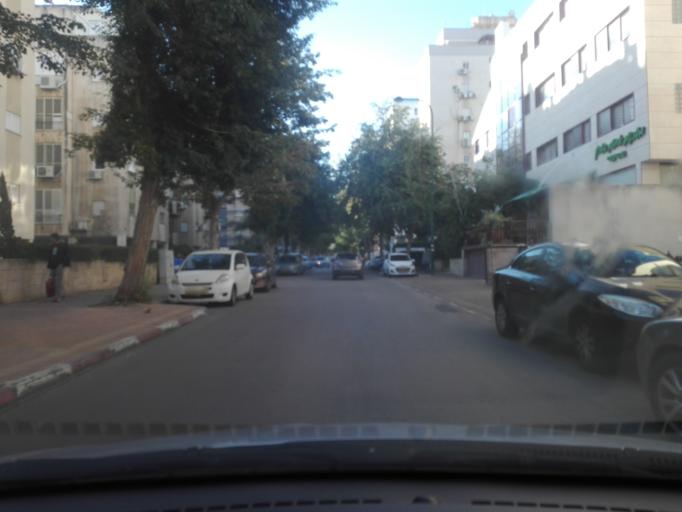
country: IL
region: Central District
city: Netanya
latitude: 32.3220
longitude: 34.8516
